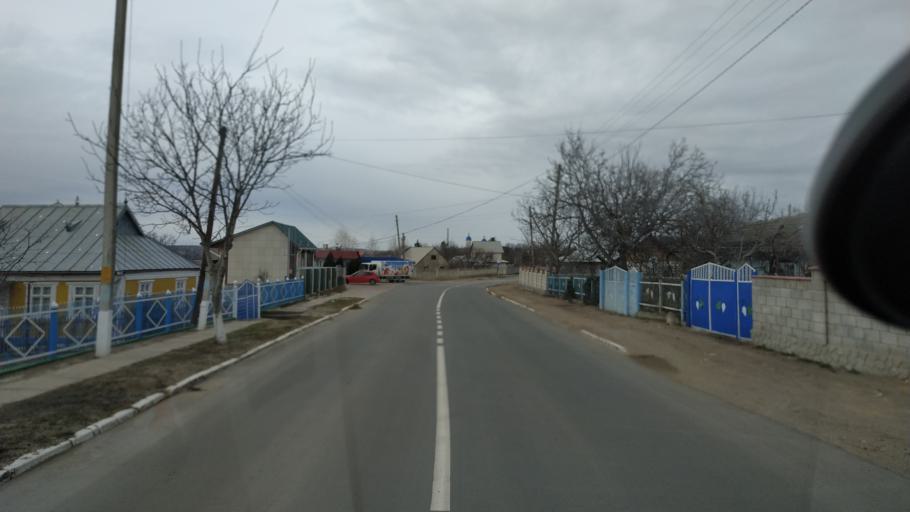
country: MD
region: Telenesti
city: Cocieri
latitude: 47.3043
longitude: 29.1127
